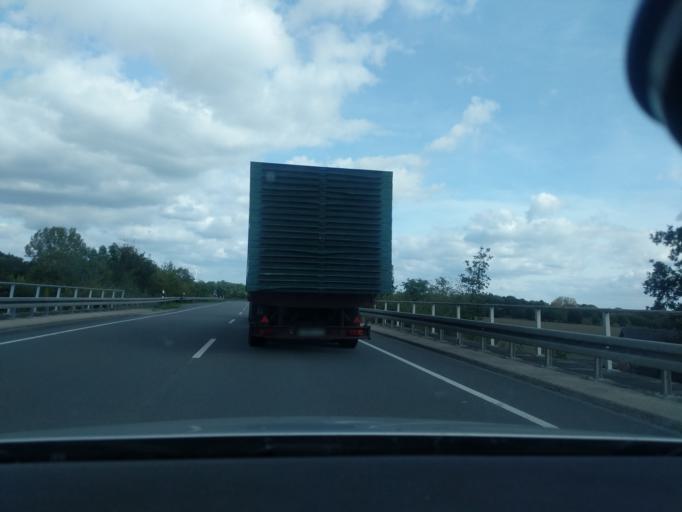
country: DE
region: Lower Saxony
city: Bohmte
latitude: 52.3754
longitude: 8.3055
